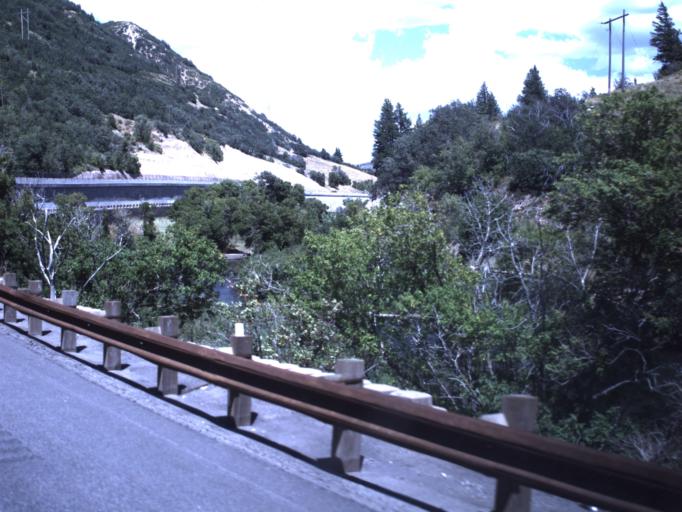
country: US
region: Utah
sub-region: Utah County
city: Orem
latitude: 40.3743
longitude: -111.5559
